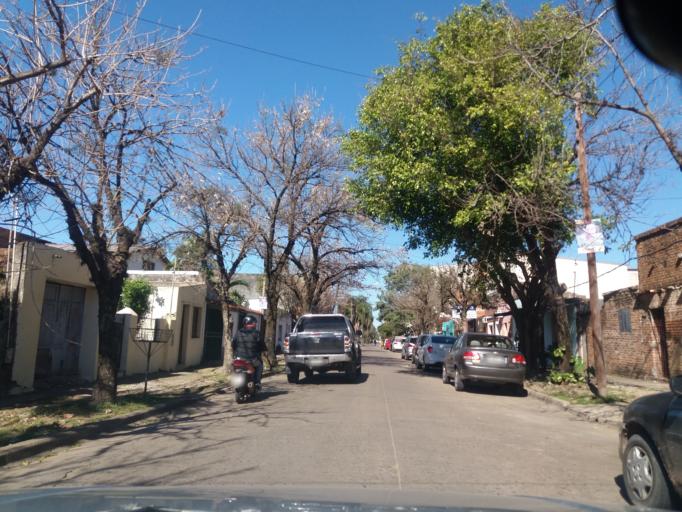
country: AR
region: Corrientes
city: Corrientes
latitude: -27.4727
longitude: -58.8194
